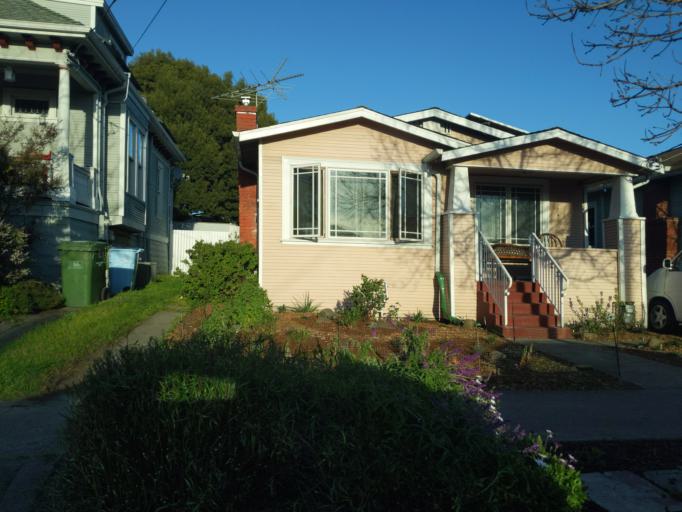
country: US
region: California
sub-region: Alameda County
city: Berkeley
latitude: 37.8559
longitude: -122.2858
